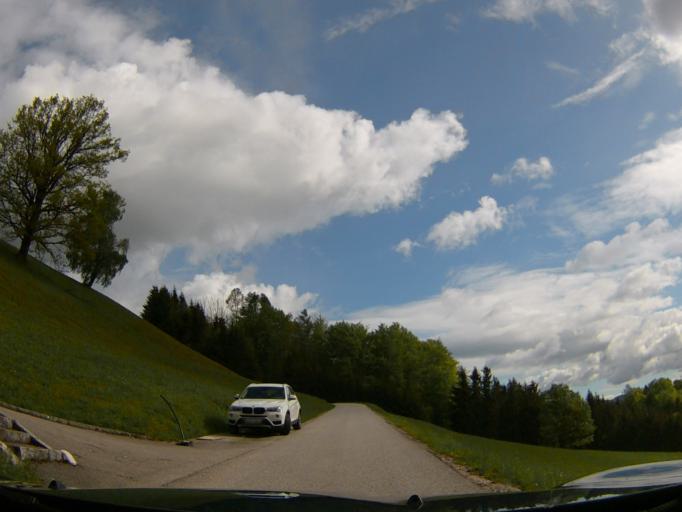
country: AT
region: Upper Austria
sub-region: Politischer Bezirk Vocklabruck
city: Steinbach am Attersee
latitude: 47.8248
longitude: 13.5039
